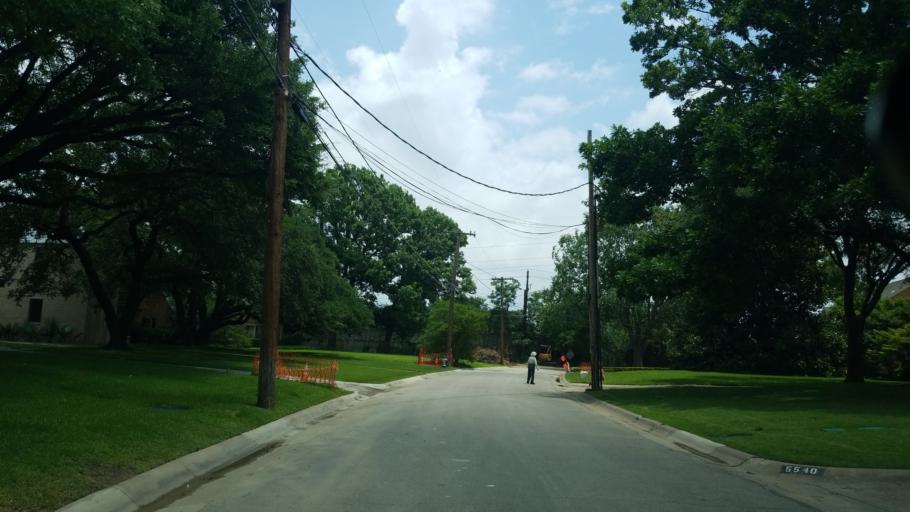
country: US
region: Texas
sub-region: Dallas County
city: University Park
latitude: 32.8429
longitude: -96.8154
